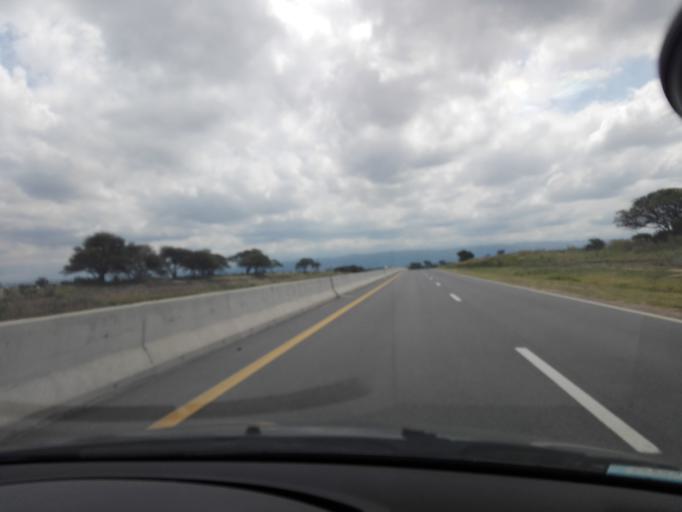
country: AR
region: Cordoba
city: Alta Gracia
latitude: -31.6522
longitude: -64.3252
